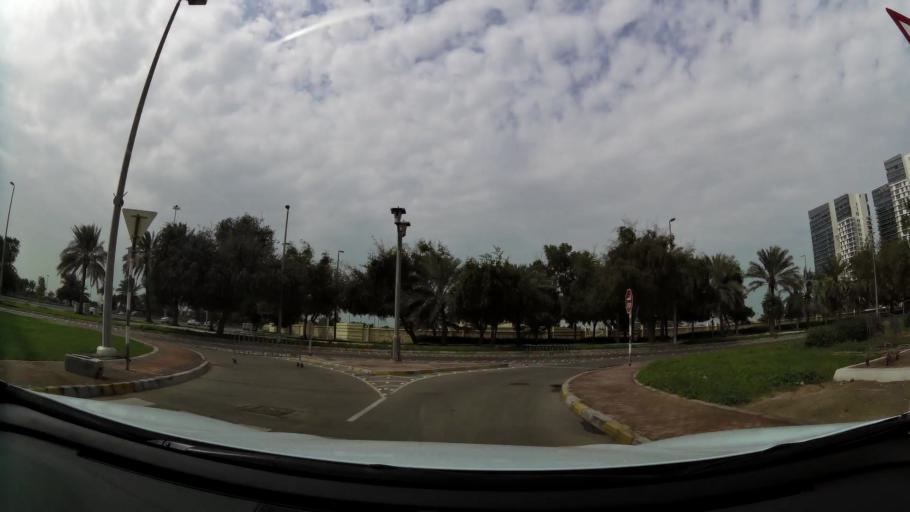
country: AE
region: Abu Dhabi
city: Abu Dhabi
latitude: 24.4106
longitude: 54.4634
